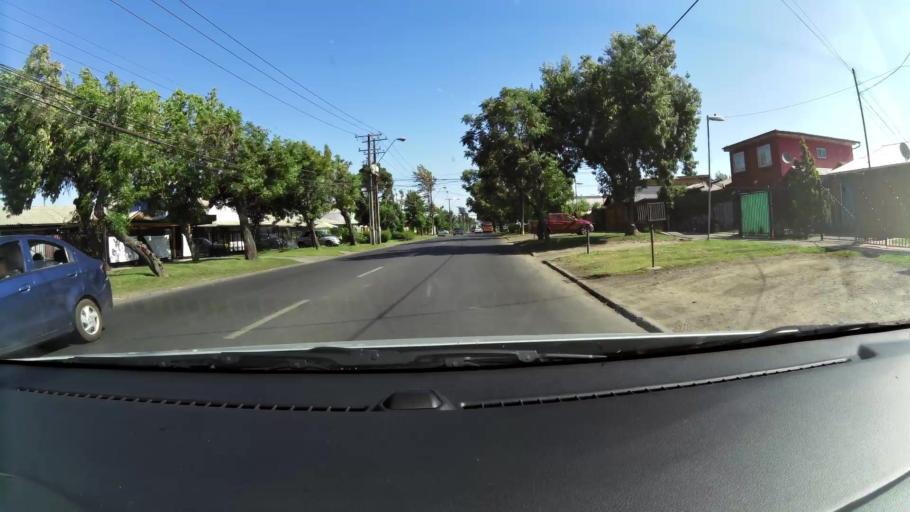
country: CL
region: Santiago Metropolitan
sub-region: Provincia de Santiago
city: Lo Prado
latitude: -33.5251
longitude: -70.7753
